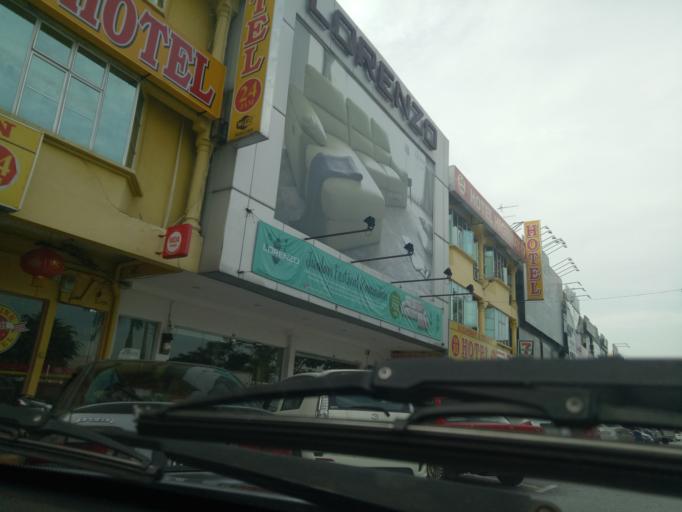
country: MY
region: Perak
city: Ipoh
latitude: 4.6204
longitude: 101.1165
